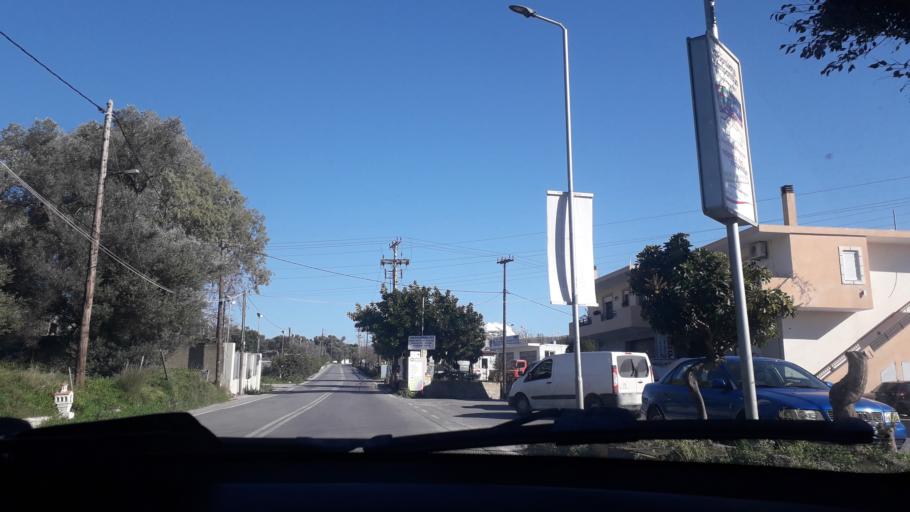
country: GR
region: Crete
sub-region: Nomos Rethymnis
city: Rethymno
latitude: 35.3609
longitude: 24.5463
